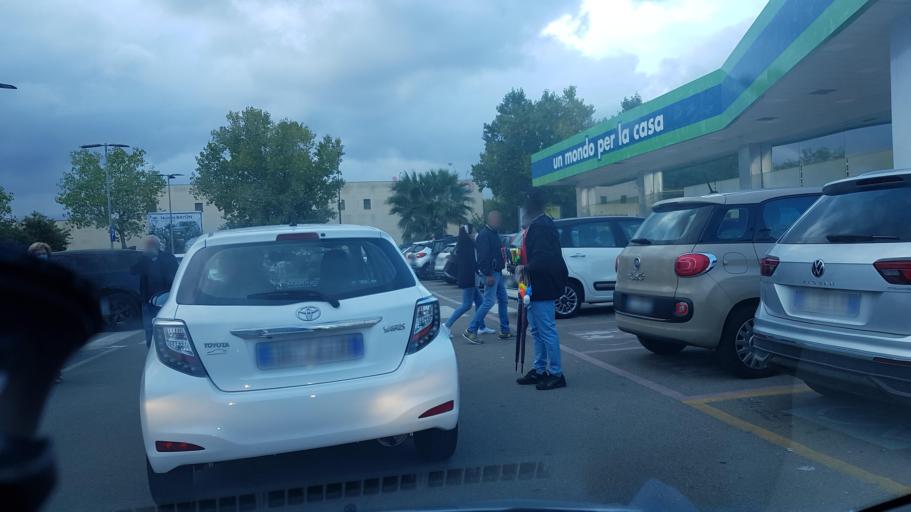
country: IT
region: Apulia
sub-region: Provincia di Lecce
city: Giorgilorio
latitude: 40.3749
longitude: 18.1463
